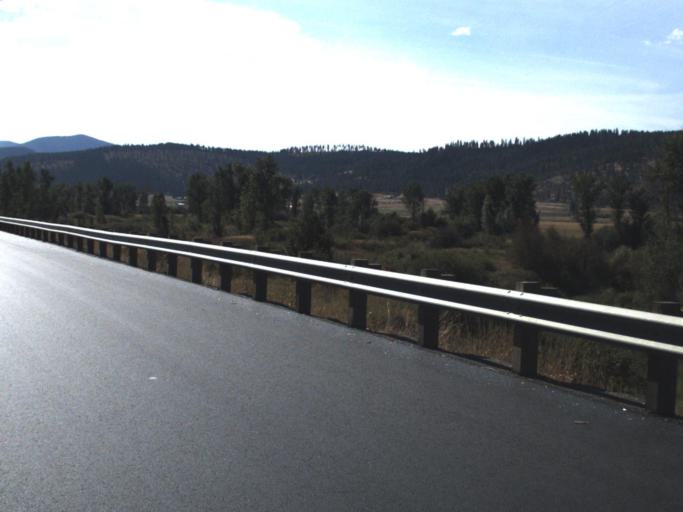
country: US
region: Washington
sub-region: Stevens County
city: Colville
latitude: 48.5097
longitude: -117.9014
